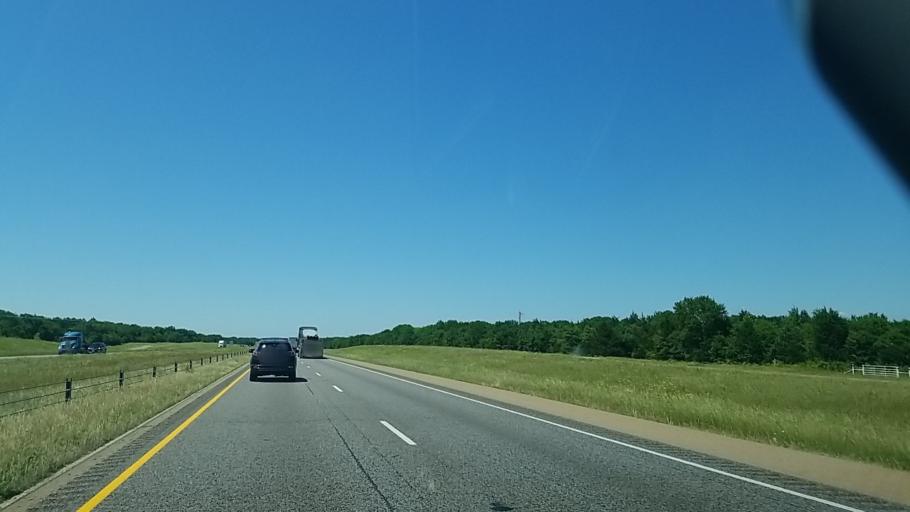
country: US
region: Texas
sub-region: Freestone County
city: Fairfield
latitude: 31.6094
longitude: -96.1564
